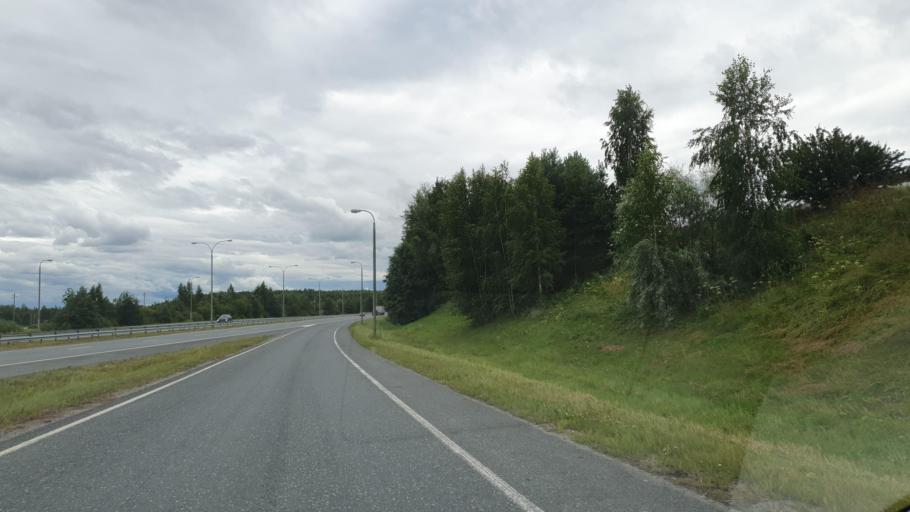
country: FI
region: Northern Savo
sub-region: Ylae-Savo
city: Iisalmi
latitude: 63.5232
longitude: 27.2496
